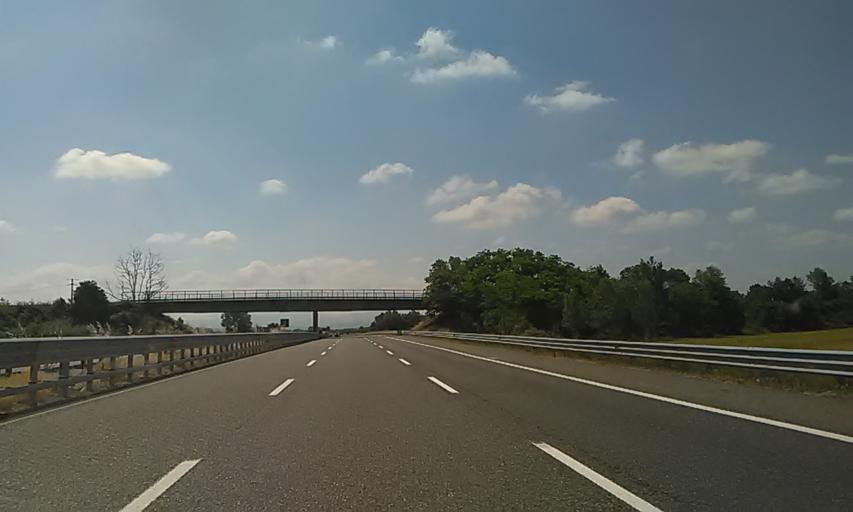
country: IT
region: Piedmont
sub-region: Provincia di Alessandria
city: Predosa
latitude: 44.7710
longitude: 8.6300
